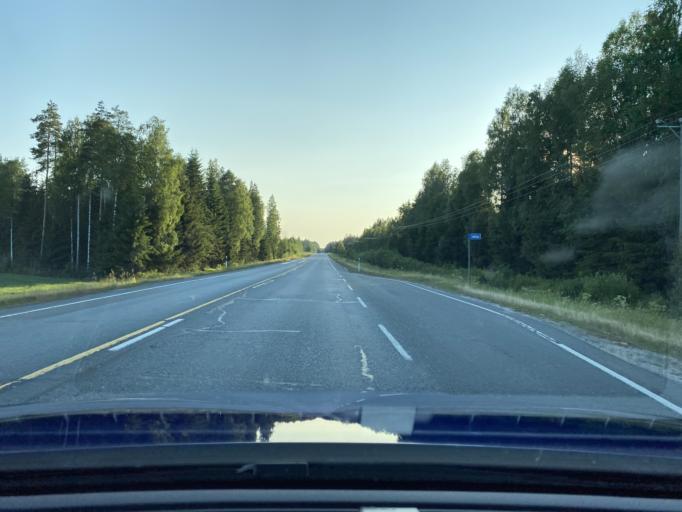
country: FI
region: Haeme
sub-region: Forssa
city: Tammela
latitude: 60.8255
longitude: 23.9623
